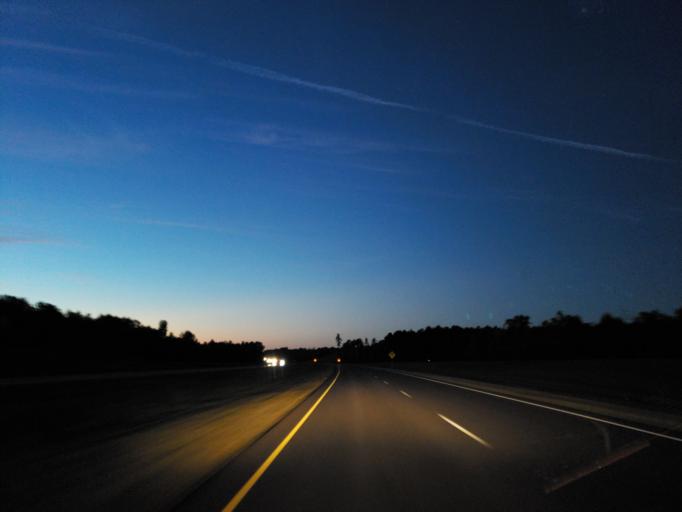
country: US
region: Mississippi
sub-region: Clarke County
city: Quitman
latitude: 32.0610
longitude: -88.6788
